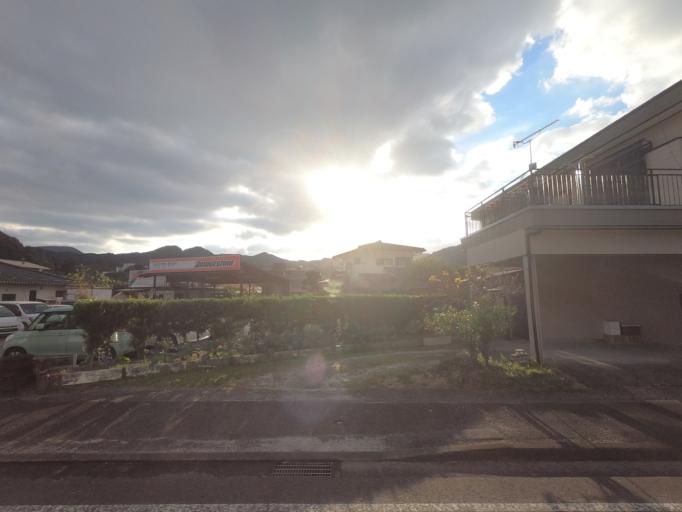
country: JP
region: Kumamoto
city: Minamata
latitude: 32.2702
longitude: 130.5031
